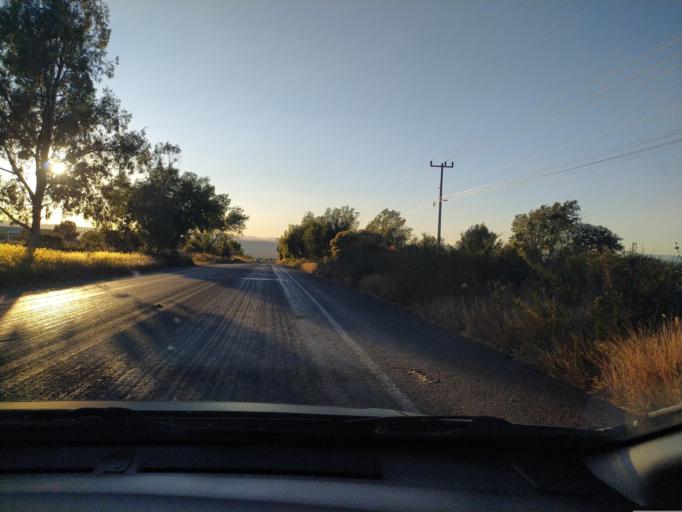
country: MX
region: Jalisco
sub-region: San Julian
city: Colonia Veintitres de Mayo
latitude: 21.0090
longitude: -102.2520
